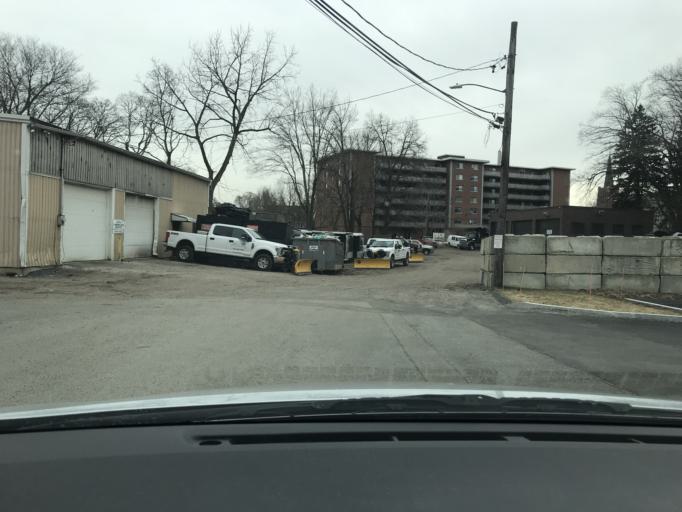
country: US
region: Massachusetts
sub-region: Middlesex County
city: Arlington
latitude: 42.4182
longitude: -71.1501
